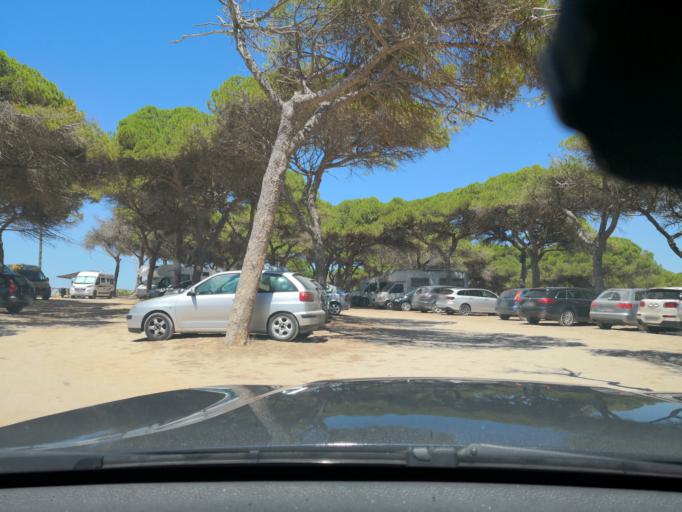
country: PT
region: Faro
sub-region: Loule
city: Quarteira
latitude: 37.0596
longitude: -8.0839
